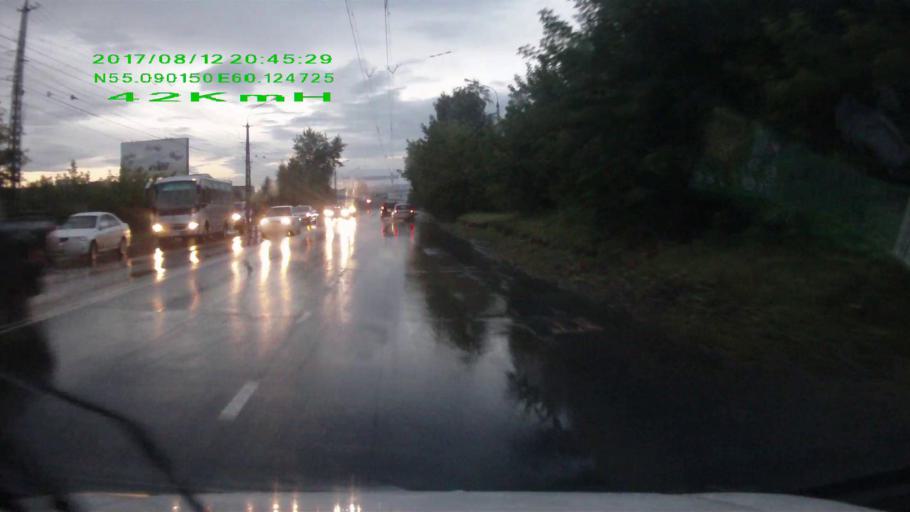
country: RU
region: Chelyabinsk
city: Miass
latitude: 55.0902
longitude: 60.1247
